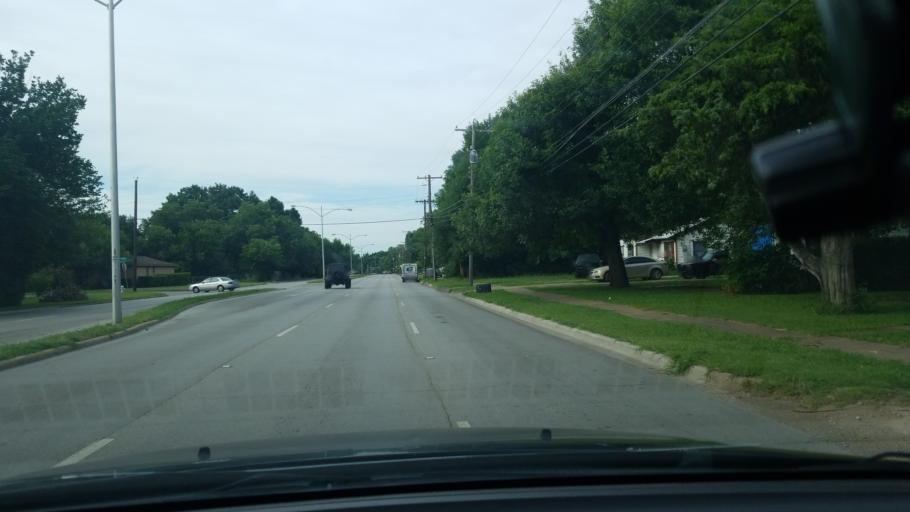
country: US
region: Texas
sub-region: Dallas County
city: Balch Springs
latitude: 32.7591
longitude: -96.6655
